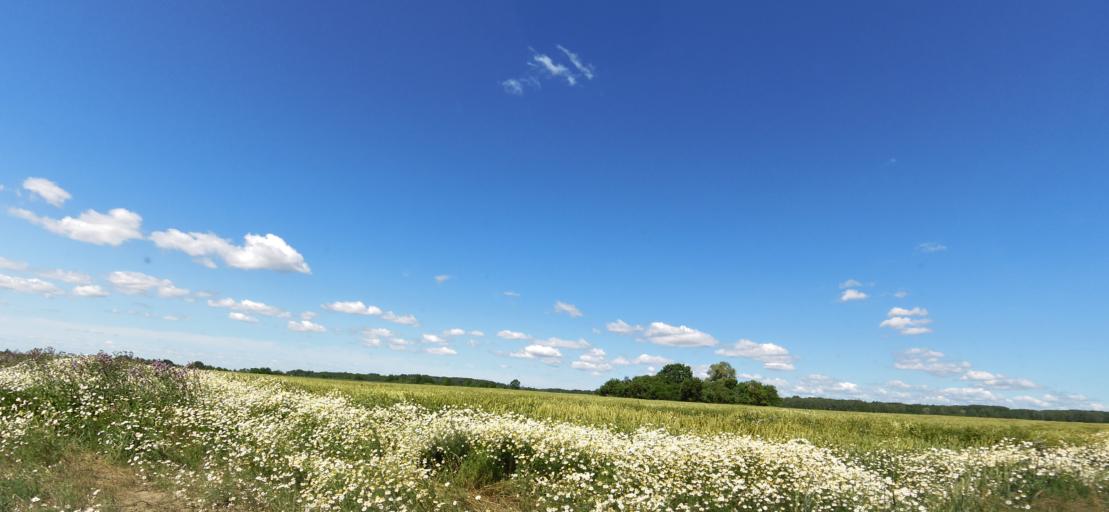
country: LT
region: Panevezys
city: Pasvalys
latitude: 56.2730
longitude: 24.5134
